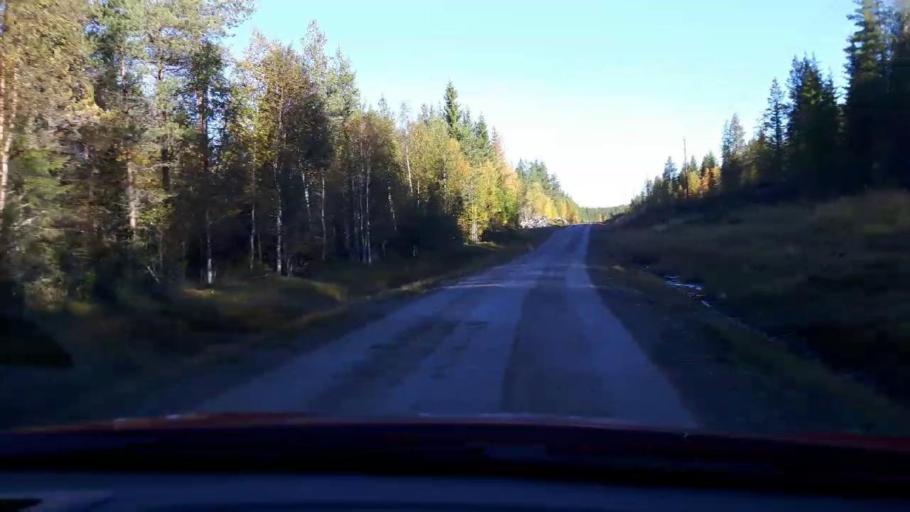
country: SE
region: Jaemtland
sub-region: Stroemsunds Kommun
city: Stroemsund
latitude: 64.3743
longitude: 15.1517
